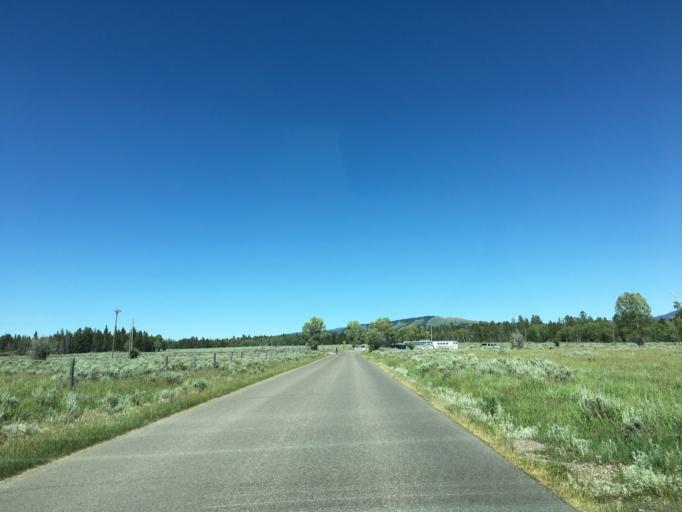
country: US
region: Wyoming
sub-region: Teton County
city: Moose Wilson Road
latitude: 43.5989
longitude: -110.7998
